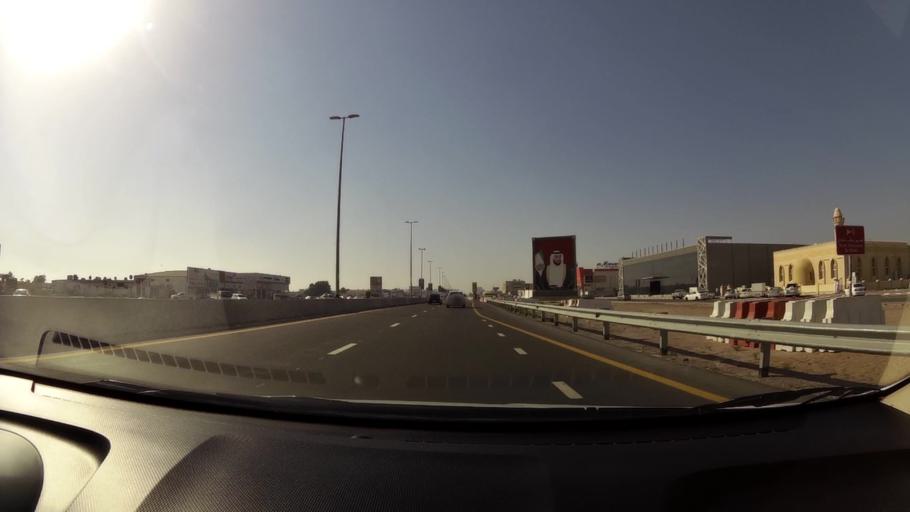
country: AE
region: Umm al Qaywayn
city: Umm al Qaywayn
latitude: 25.5008
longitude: 55.5504
